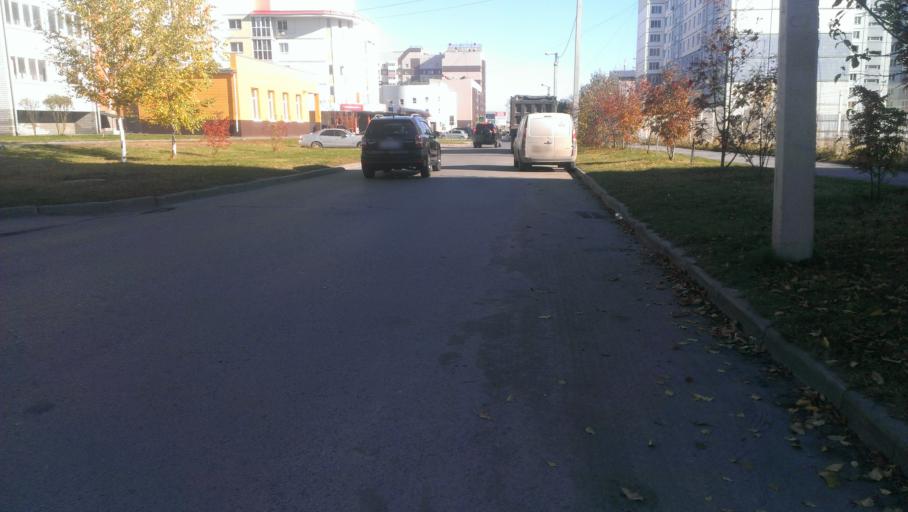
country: RU
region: Altai Krai
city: Novosilikatnyy
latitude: 53.3296
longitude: 83.6866
